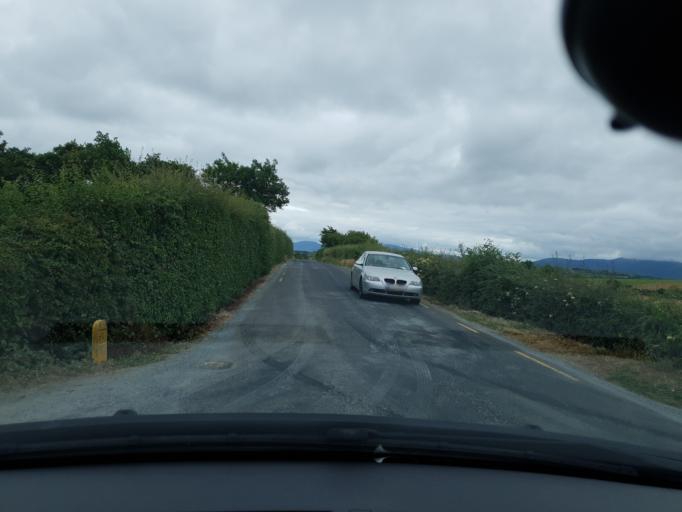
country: IE
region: Munster
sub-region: Ciarrai
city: Cill Airne
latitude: 52.1422
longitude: -9.5886
